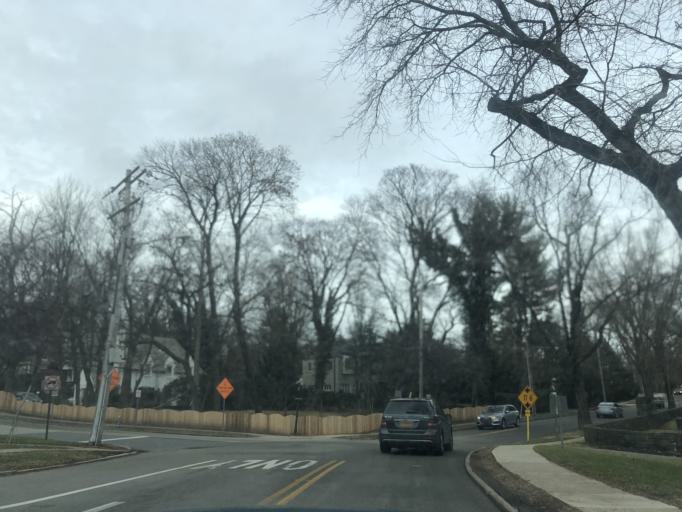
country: US
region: Pennsylvania
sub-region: Montgomery County
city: Bryn Mawr
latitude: 40.0273
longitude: -75.3296
